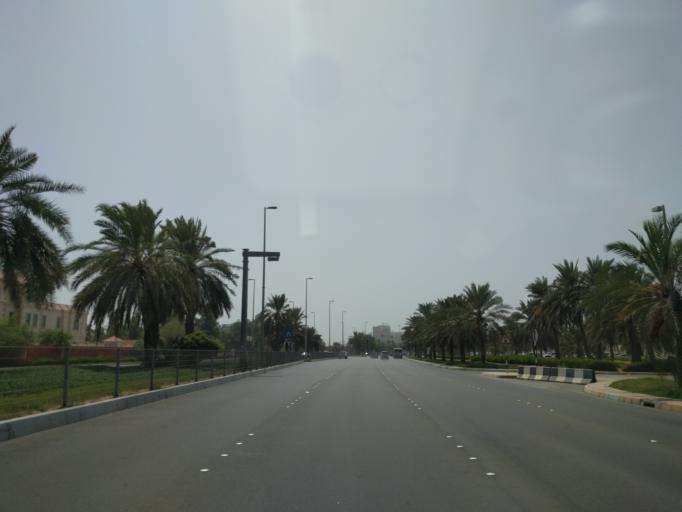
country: AE
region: Abu Dhabi
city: Abu Dhabi
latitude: 24.4353
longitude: 54.4235
